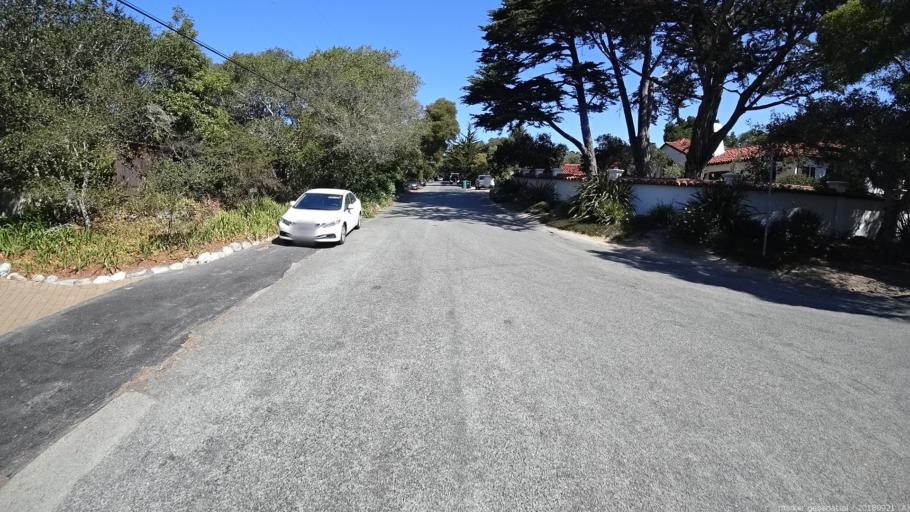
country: US
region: California
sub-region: Monterey County
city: Carmel-by-the-Sea
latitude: 36.5512
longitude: -121.9125
